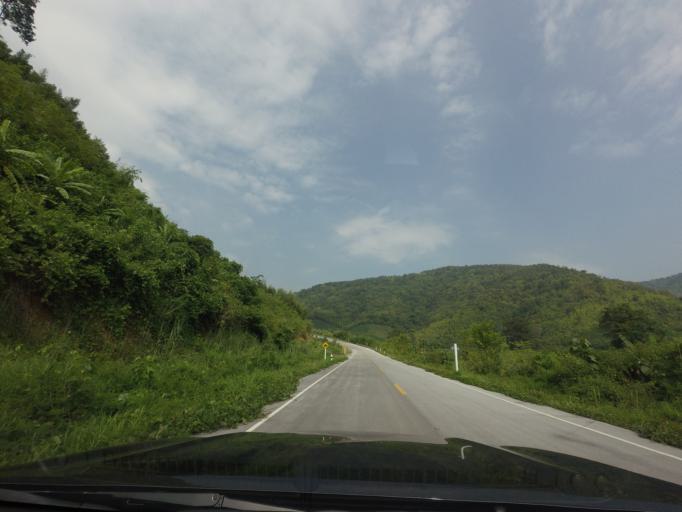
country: LA
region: Xiagnabouli
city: Muang Kenthao
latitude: 17.7743
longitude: 101.5243
